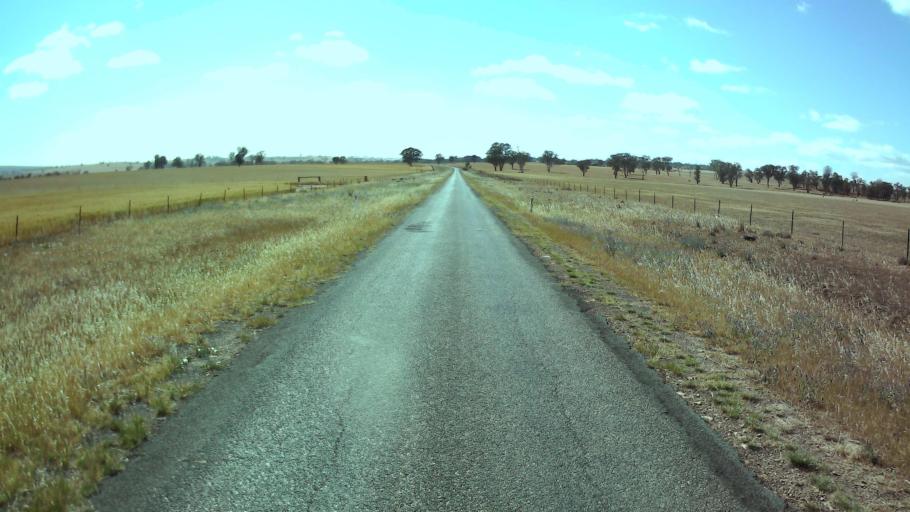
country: AU
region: New South Wales
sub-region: Young
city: Young
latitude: -34.0725
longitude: 148.3420
